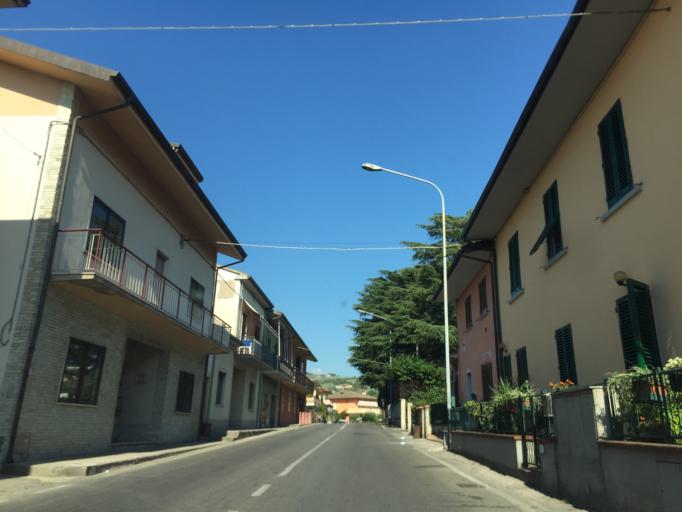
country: IT
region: Tuscany
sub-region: Provincia di Pistoia
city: Monsummano Terme
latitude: 43.8606
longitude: 10.8203
